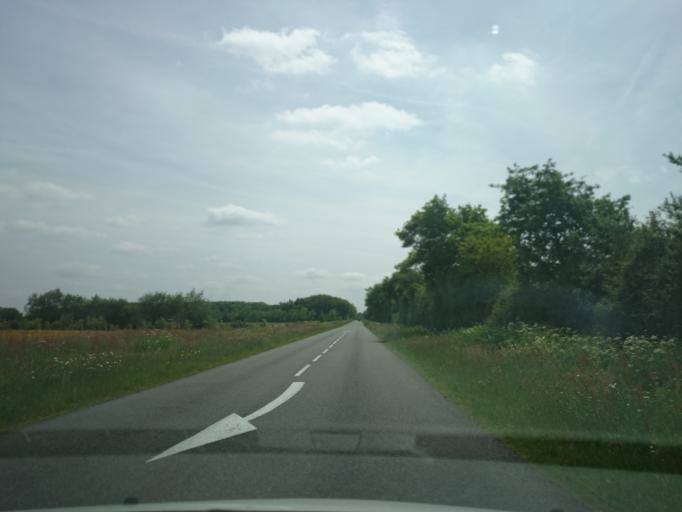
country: FR
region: Pays de la Loire
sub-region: Departement de la Loire-Atlantique
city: La Montagne
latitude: 47.1642
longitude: -1.6722
